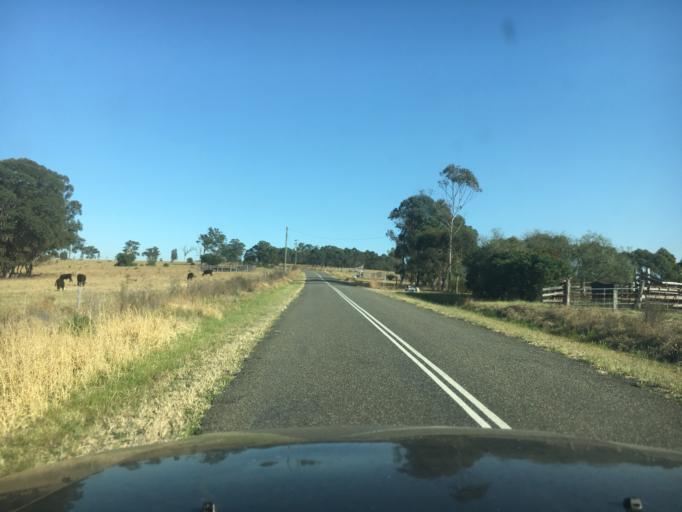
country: AU
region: New South Wales
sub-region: Singleton
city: Singleton
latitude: -32.5517
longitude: 151.2738
